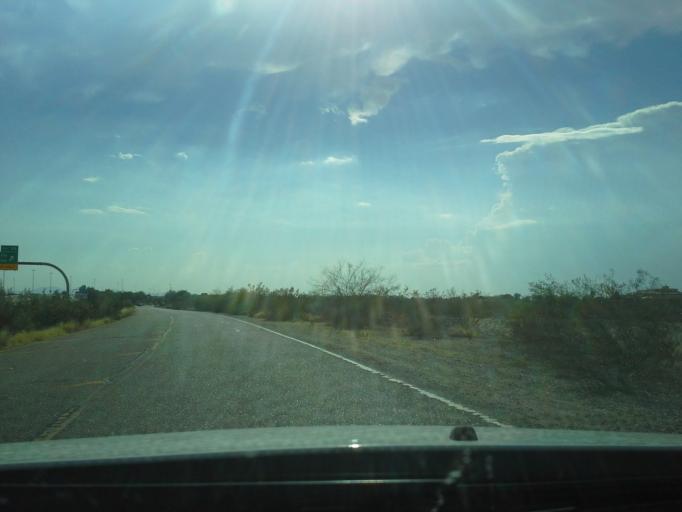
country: US
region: Arizona
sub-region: Maricopa County
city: Peoria
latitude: 33.6699
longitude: -112.1625
